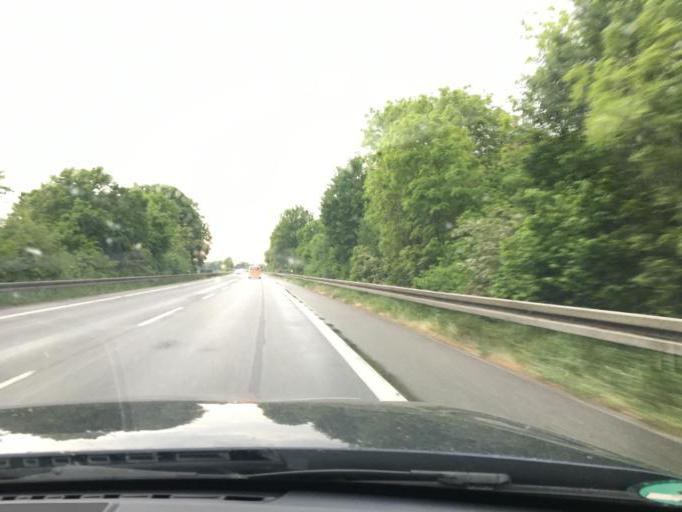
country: DE
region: North Rhine-Westphalia
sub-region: Regierungsbezirk Munster
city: Greven
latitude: 52.1246
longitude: 7.5897
